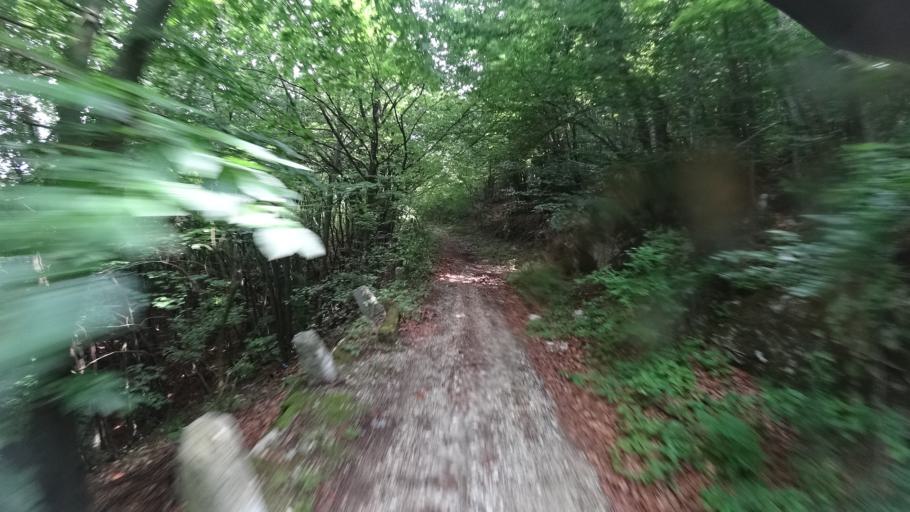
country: HR
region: Licko-Senjska
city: Jezerce
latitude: 44.8813
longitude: 15.7002
